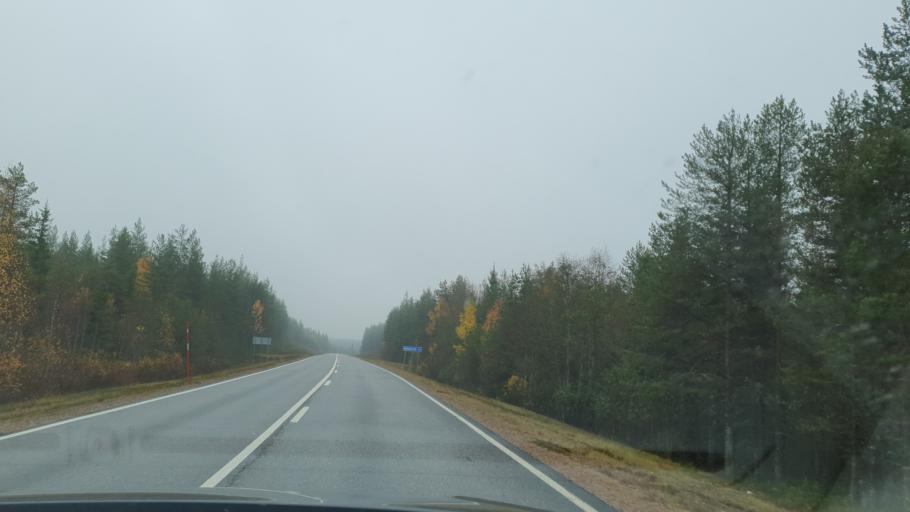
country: FI
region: Lapland
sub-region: Rovaniemi
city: Rovaniemi
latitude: 66.9464
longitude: 25.3632
